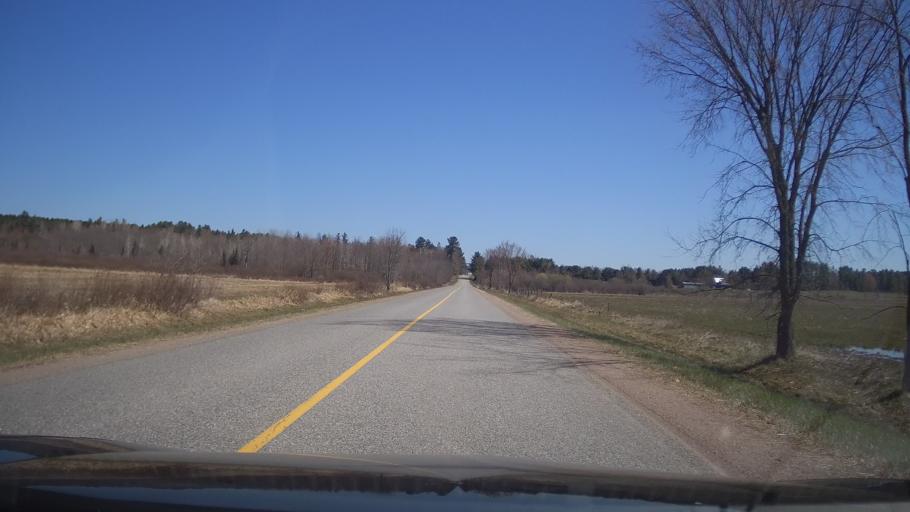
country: CA
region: Ontario
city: Arnprior
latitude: 45.5211
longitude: -76.4042
